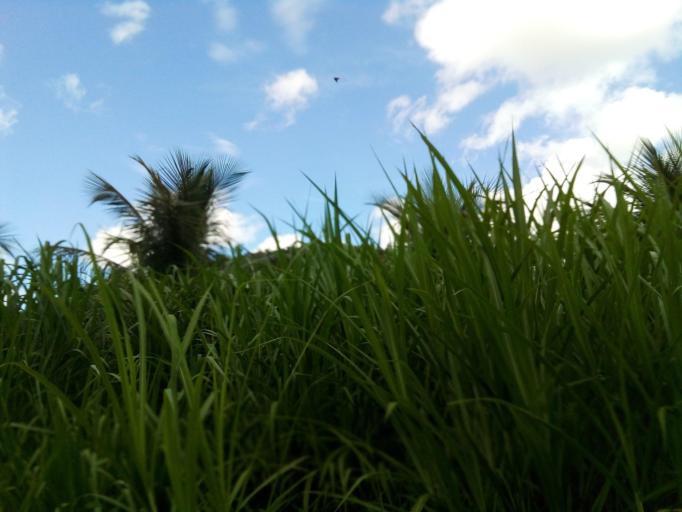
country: BR
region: Espirito Santo
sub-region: Ibiracu
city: Ibiracu
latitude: -19.8685
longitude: -40.3614
